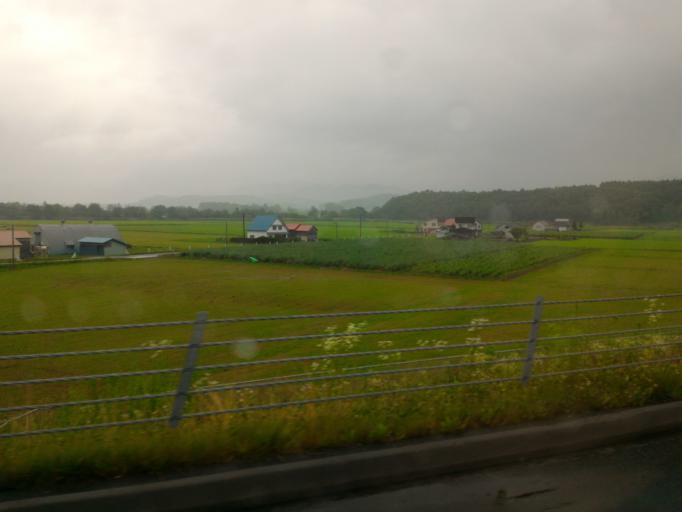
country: JP
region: Hokkaido
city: Nayoro
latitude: 44.4944
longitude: 142.3478
